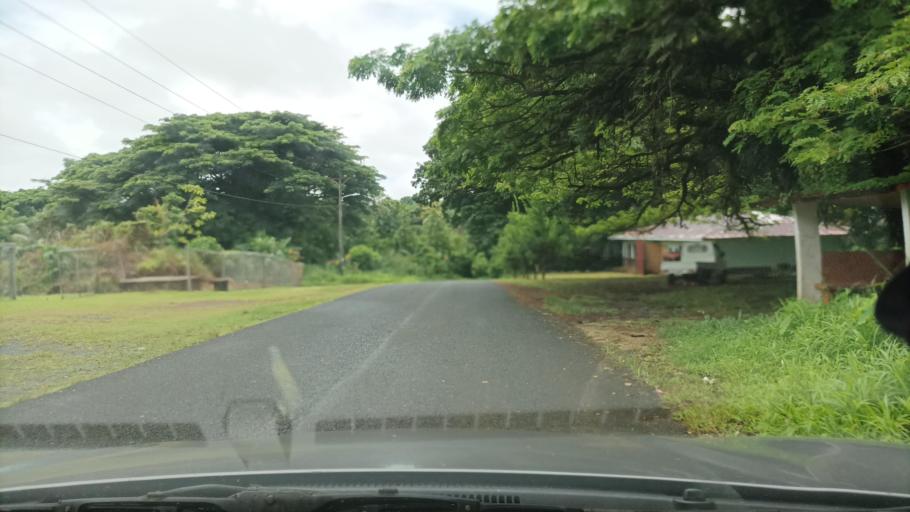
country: FM
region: Pohnpei
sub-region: Madolenihm Municipality
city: Madolenihm Municipality Government
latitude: 6.8377
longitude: 158.2987
